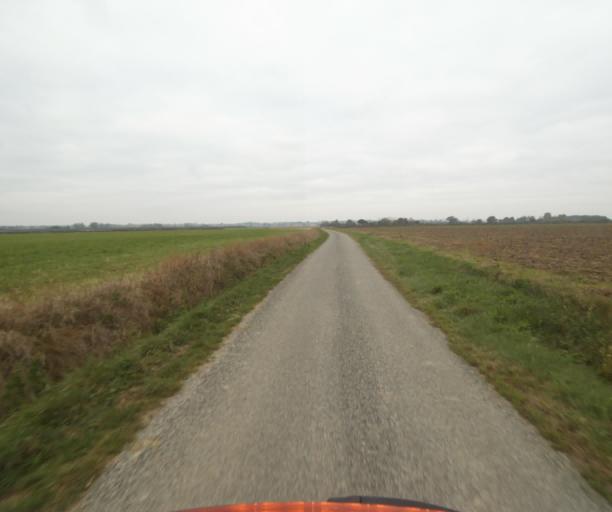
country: FR
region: Midi-Pyrenees
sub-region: Departement du Tarn-et-Garonne
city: Verdun-sur-Garonne
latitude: 43.8102
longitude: 1.2388
